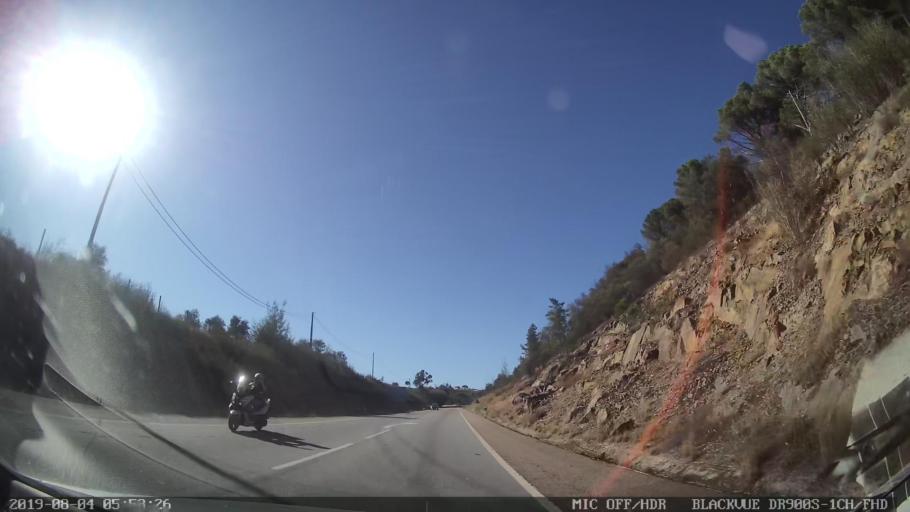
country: PT
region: Portalegre
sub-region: Gaviao
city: Gaviao
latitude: 39.4542
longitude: -7.9292
